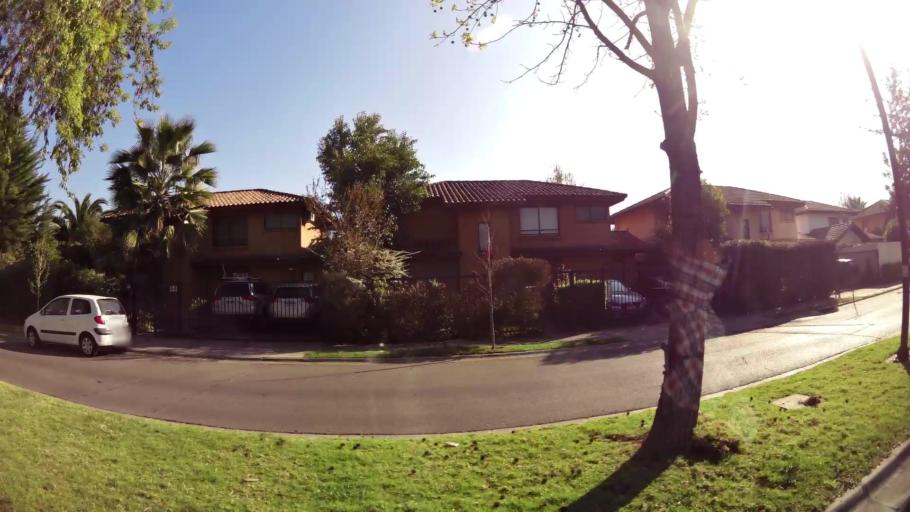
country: CL
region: Santiago Metropolitan
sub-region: Provincia de Chacabuco
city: Chicureo Abajo
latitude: -33.3557
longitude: -70.6679
